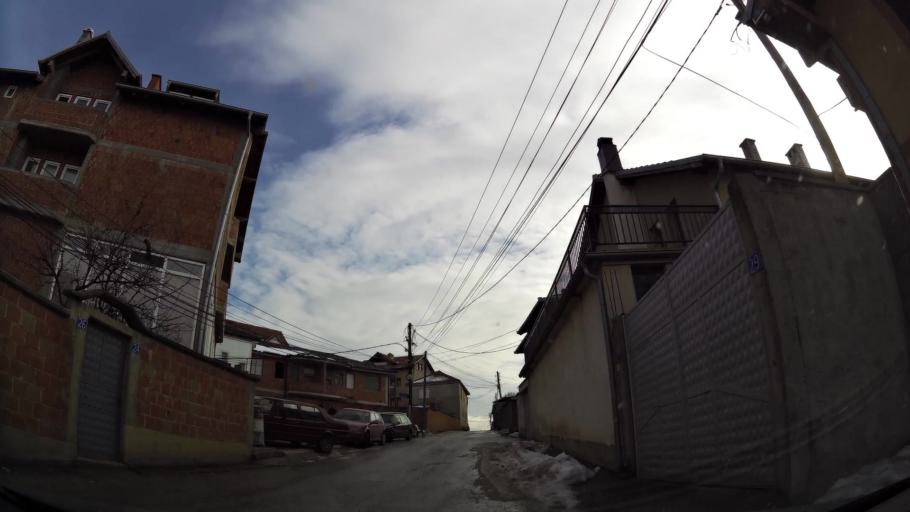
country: XK
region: Pristina
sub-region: Komuna e Prishtines
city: Pristina
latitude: 42.6847
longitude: 21.1544
